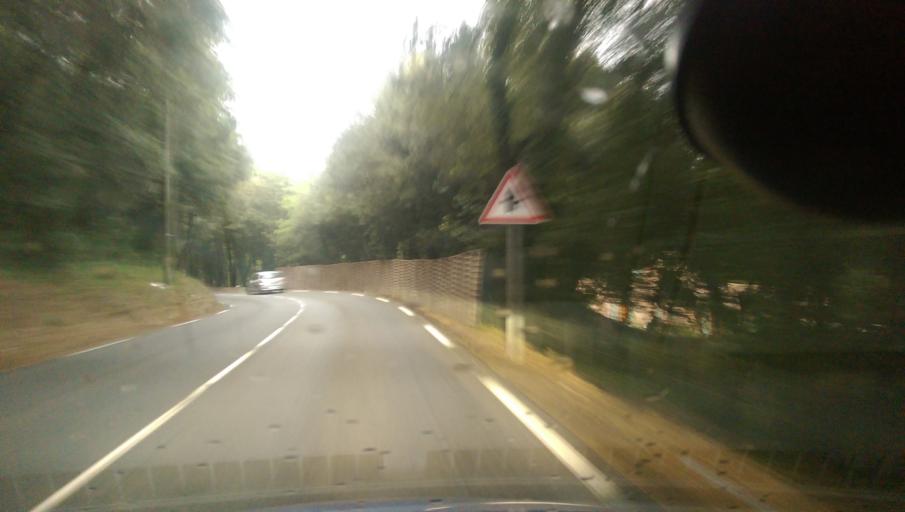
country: FR
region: Provence-Alpes-Cote d'Azur
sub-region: Departement des Alpes-Maritimes
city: Chateauneuf-Grasse
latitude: 43.6572
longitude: 7.0012
